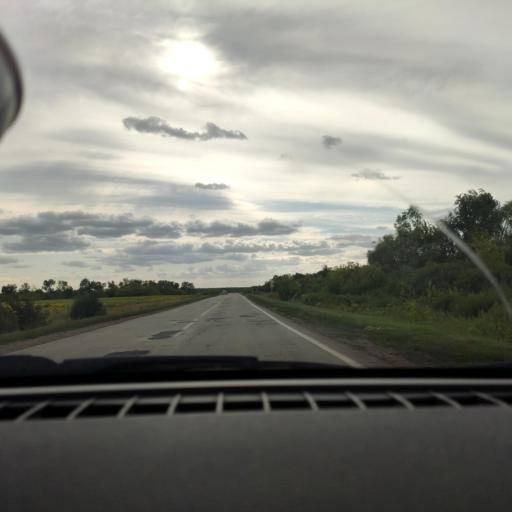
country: RU
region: Samara
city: Krasnyy Yar
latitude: 53.4323
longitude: 50.5520
